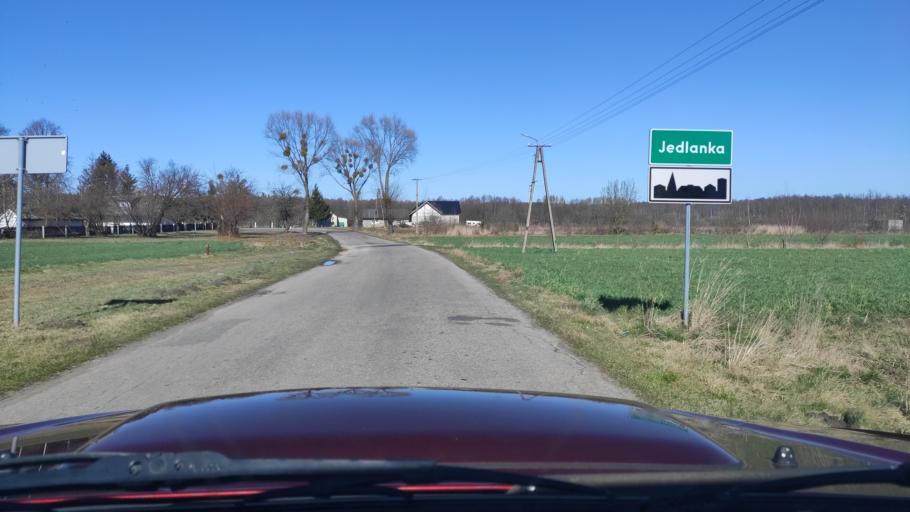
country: PL
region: Masovian Voivodeship
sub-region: Powiat zwolenski
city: Zwolen
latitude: 51.3834
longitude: 21.5778
